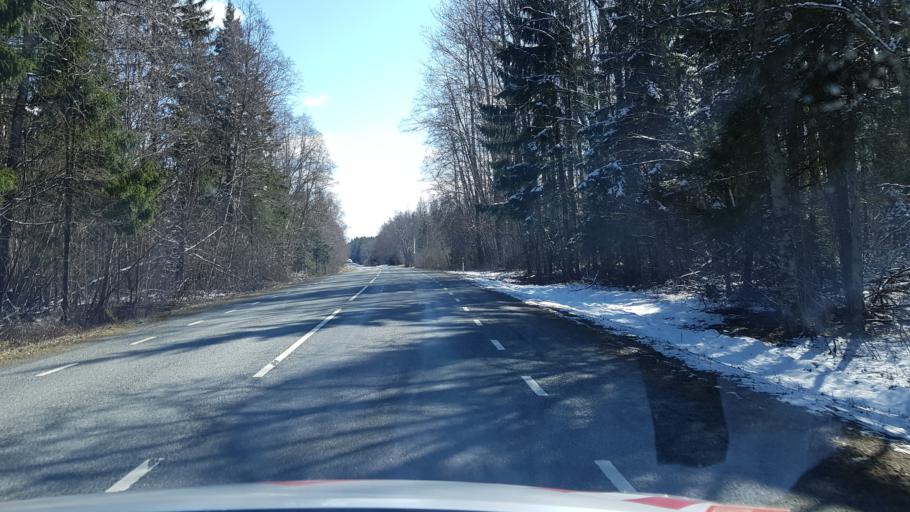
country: EE
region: Laeaene-Virumaa
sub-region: Tapa vald
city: Tapa
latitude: 59.4369
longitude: 25.9614
